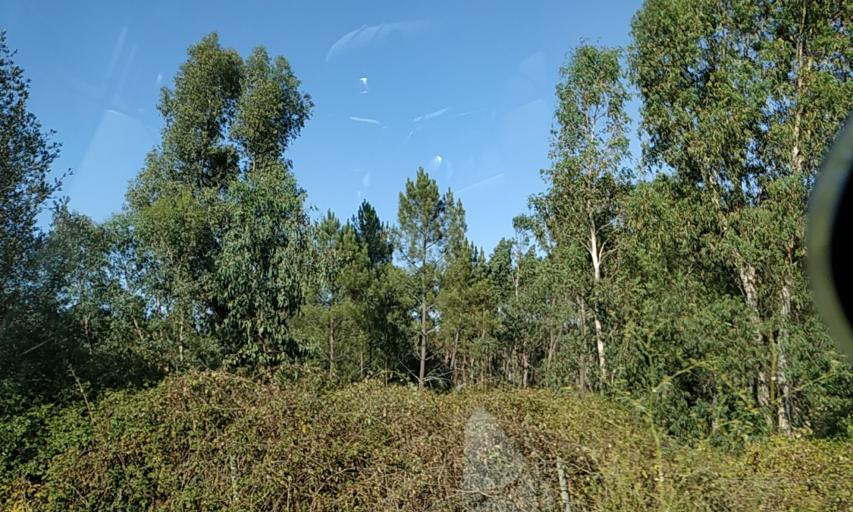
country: PT
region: Santarem
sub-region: Coruche
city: Coruche
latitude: 39.0227
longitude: -8.5618
